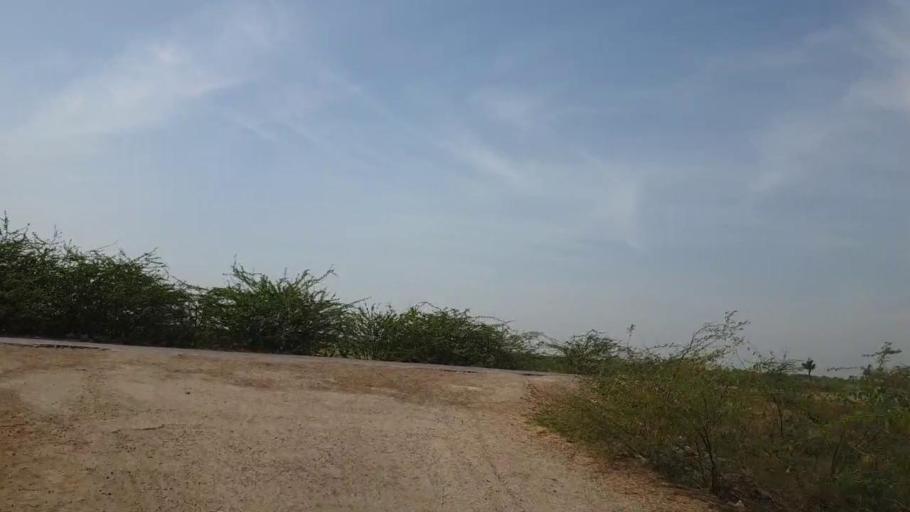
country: PK
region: Sindh
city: Kunri
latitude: 25.1948
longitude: 69.5587
